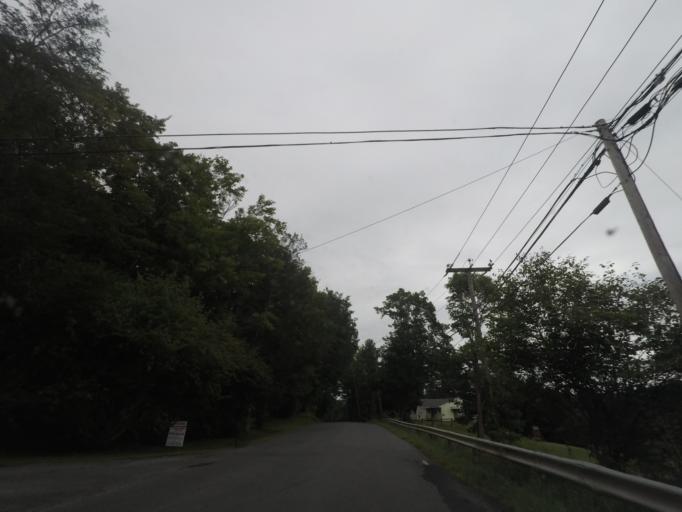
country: US
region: New York
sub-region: Columbia County
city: Chatham
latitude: 42.4139
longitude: -73.5329
